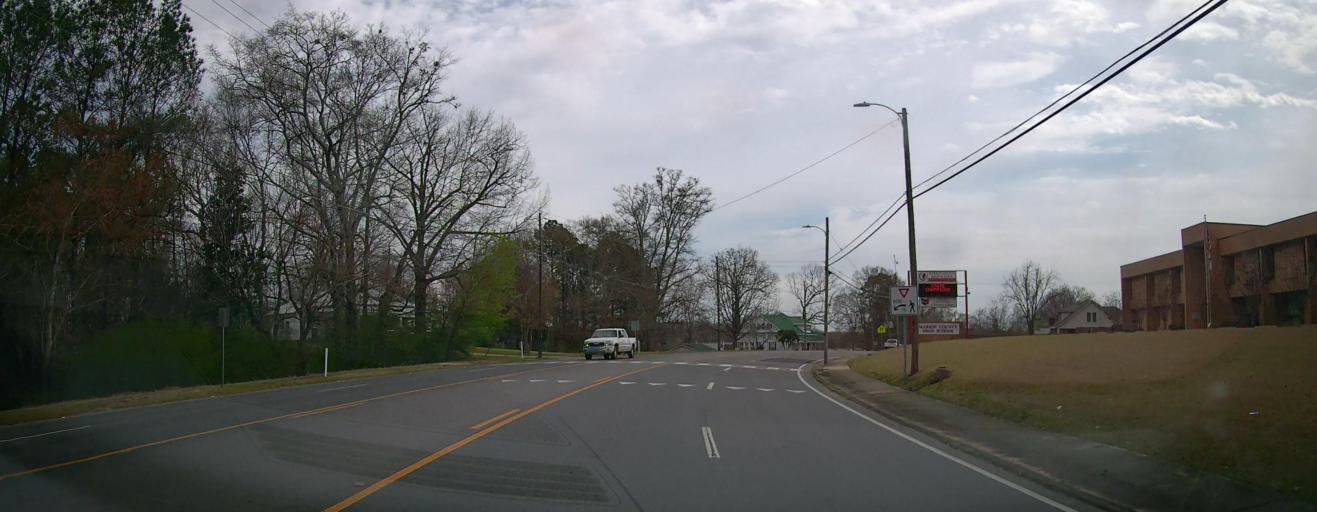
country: US
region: Alabama
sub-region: Marion County
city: Guin
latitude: 33.9744
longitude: -87.9151
